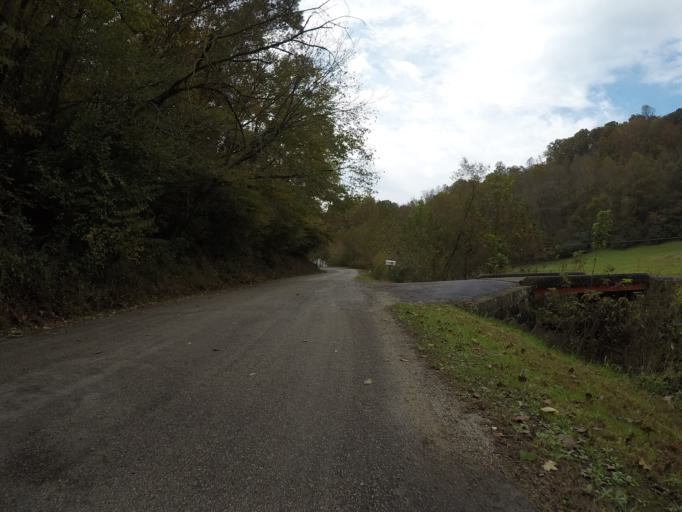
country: US
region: West Virginia
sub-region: Wayne County
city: Lavalette
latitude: 38.3380
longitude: -82.4379
